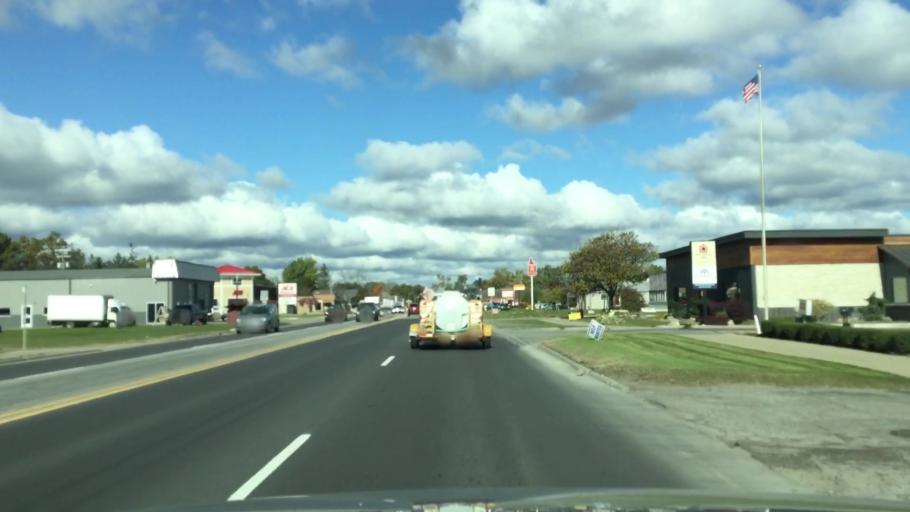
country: US
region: Michigan
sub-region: Oakland County
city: Oxford
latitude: 42.8157
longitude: -83.2566
